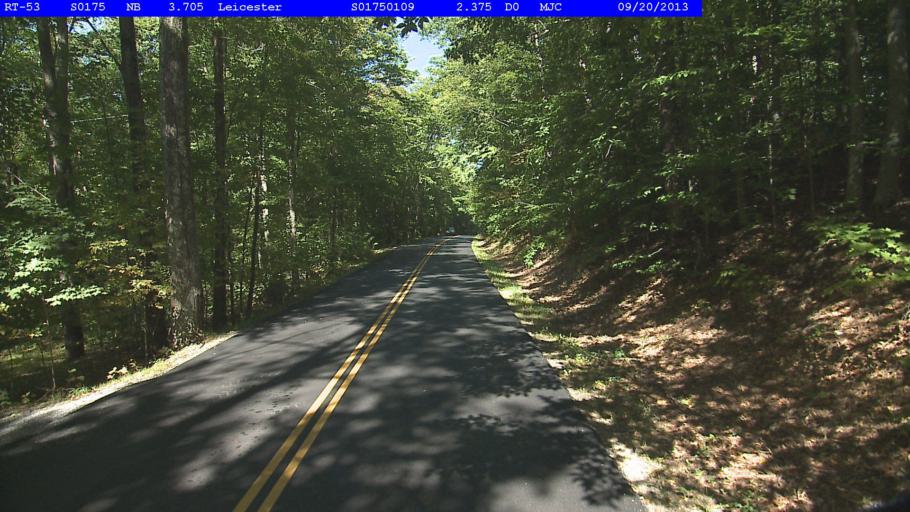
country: US
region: Vermont
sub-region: Rutland County
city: Brandon
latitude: 43.8770
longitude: -73.0639
